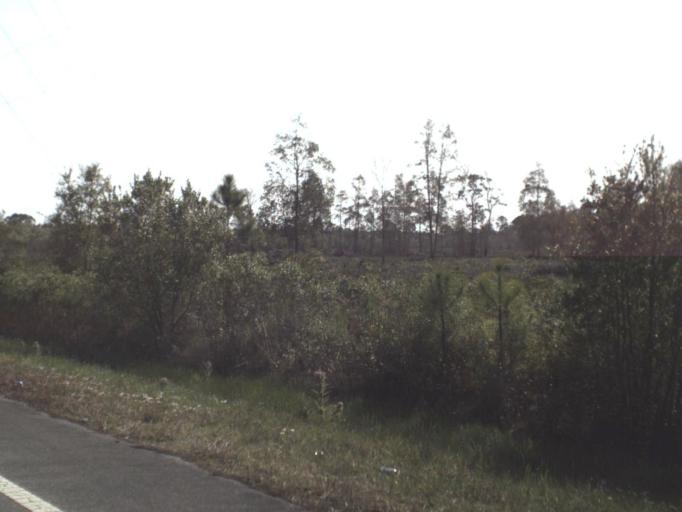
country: US
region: Florida
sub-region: Franklin County
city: Carrabelle
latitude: 29.9454
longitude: -84.5016
